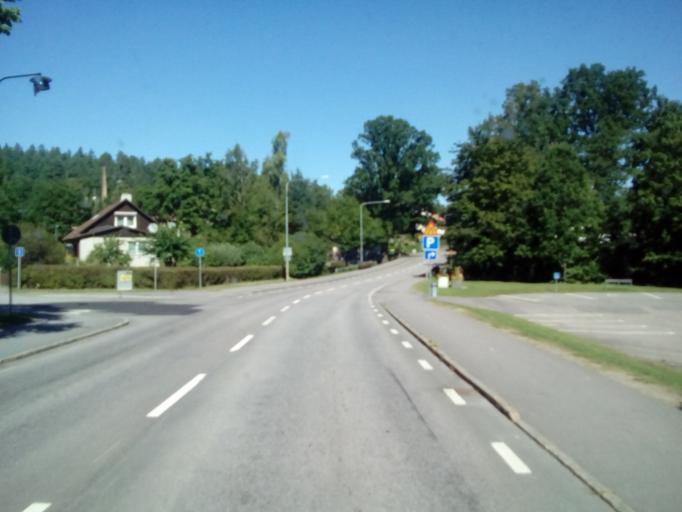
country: SE
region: OEstergoetland
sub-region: Kinda Kommun
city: Kisa
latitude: 57.9908
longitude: 15.6351
